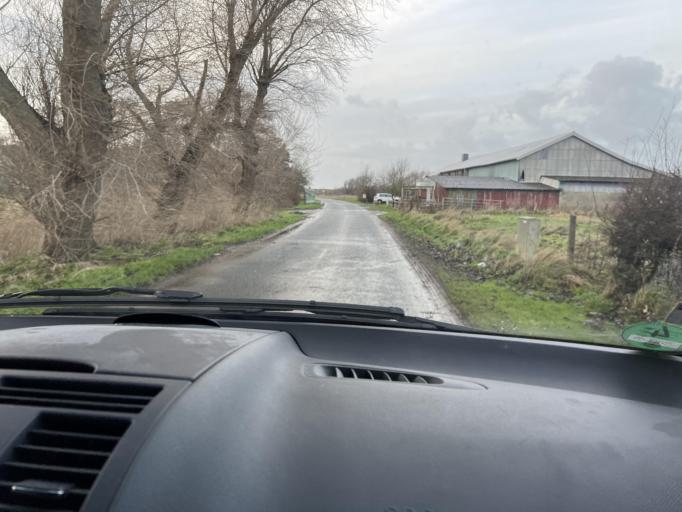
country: DE
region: Schleswig-Holstein
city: Hedwigenkoog
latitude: 54.1782
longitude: 8.8183
